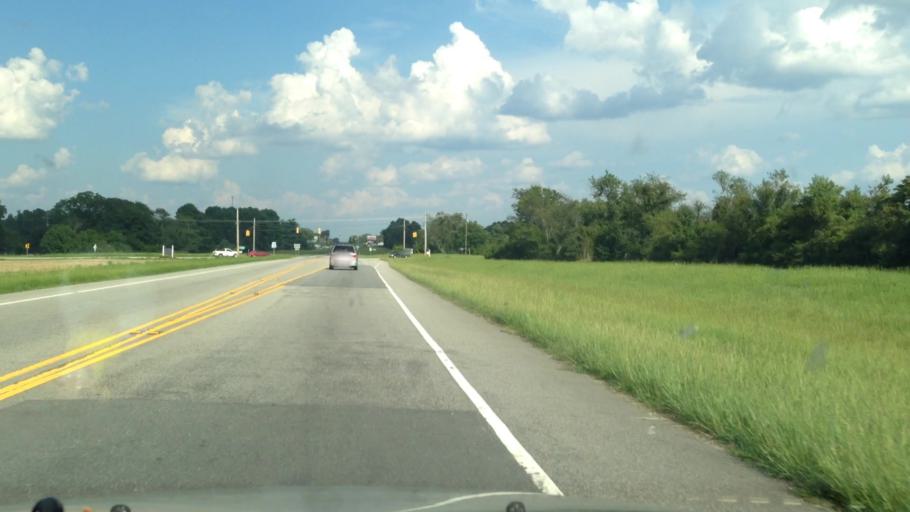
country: US
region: North Carolina
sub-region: Lee County
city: Broadway
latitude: 35.4386
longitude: -79.0387
